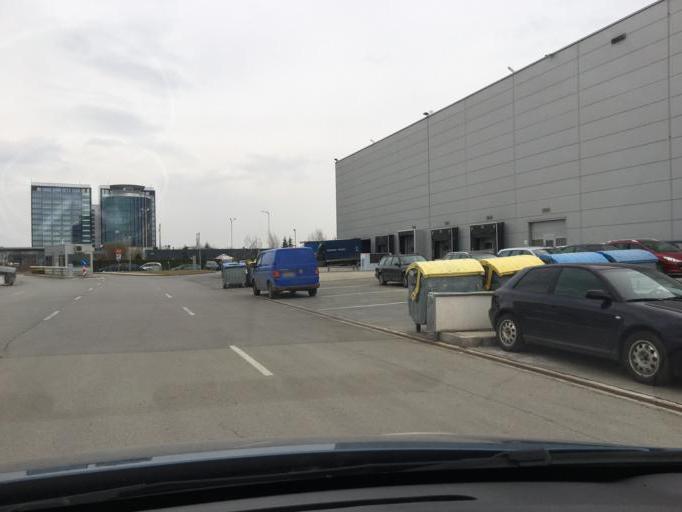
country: BG
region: Sofia-Capital
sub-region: Stolichna Obshtina
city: Sofia
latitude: 42.6798
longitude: 23.4045
